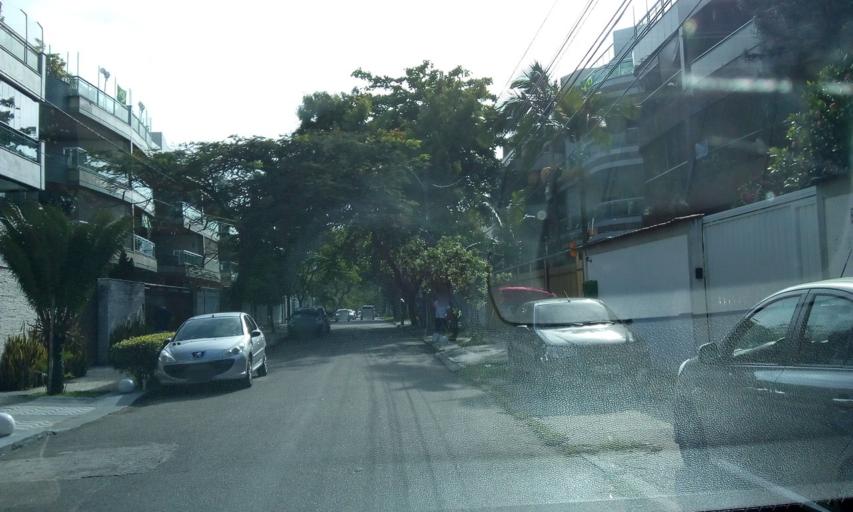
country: BR
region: Rio de Janeiro
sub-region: Nilopolis
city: Nilopolis
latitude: -23.0119
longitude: -43.4468
